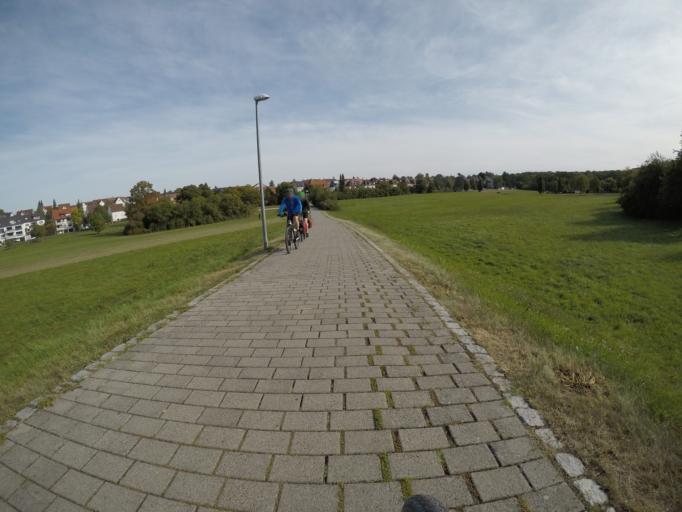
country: DE
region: Baden-Wuerttemberg
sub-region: Regierungsbezirk Stuttgart
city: Korntal
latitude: 48.8205
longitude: 9.1163
